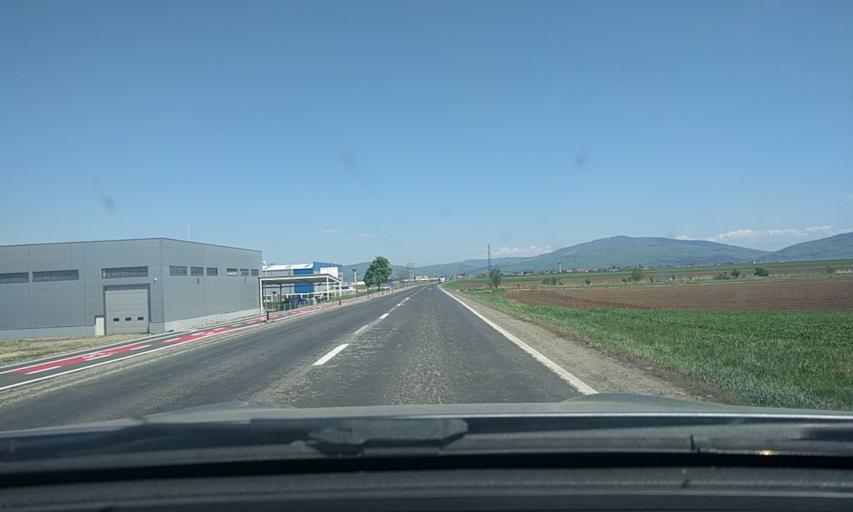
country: RO
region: Brasov
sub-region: Comuna Prejmer
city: Prejmer
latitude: 45.7150
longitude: 25.7426
